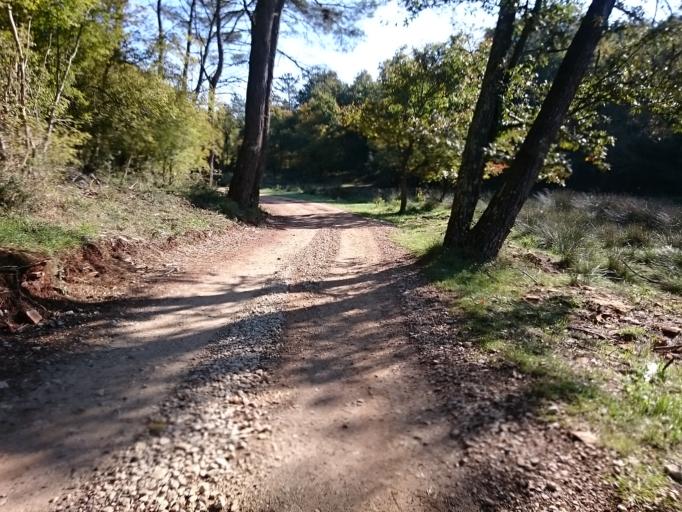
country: HR
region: Istarska
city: Novigrad
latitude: 45.2860
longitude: 13.6037
